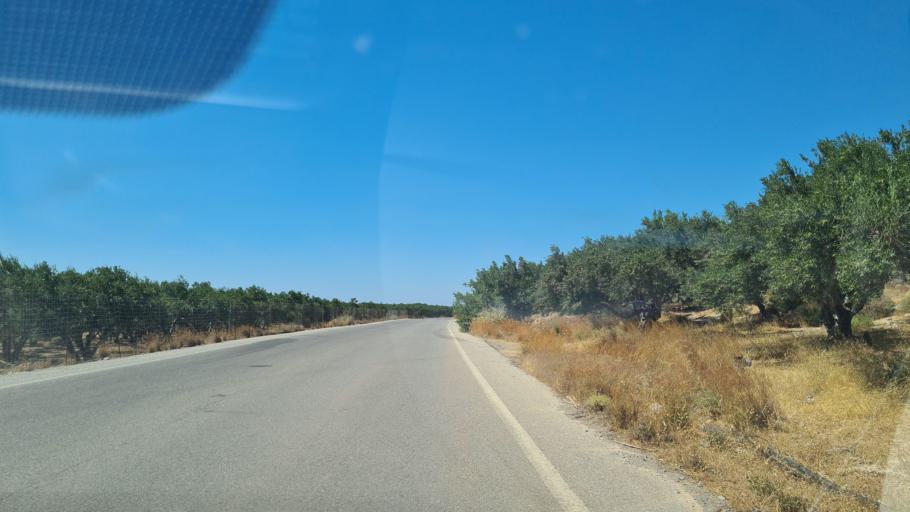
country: GR
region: Crete
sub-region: Nomos Chanias
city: Palaiochora
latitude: 35.2994
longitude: 23.5390
